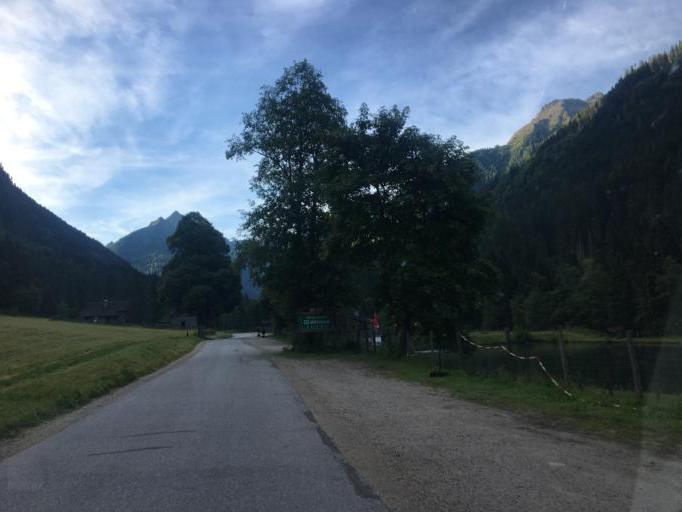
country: AT
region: Styria
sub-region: Politischer Bezirk Liezen
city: Schladming
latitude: 47.3479
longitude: 13.7269
